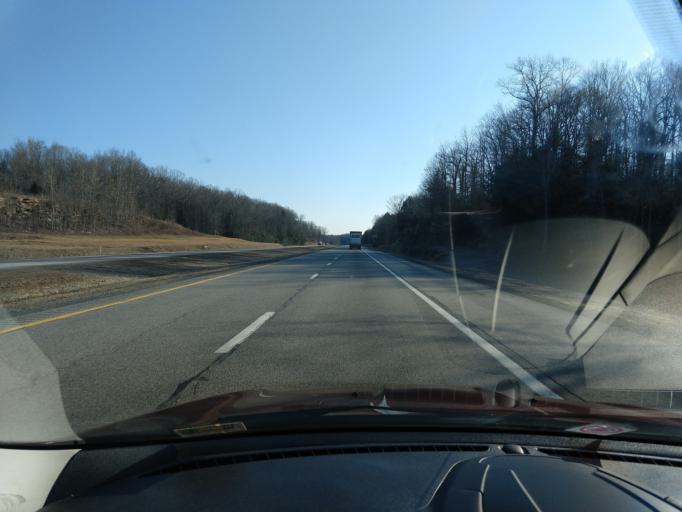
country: US
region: West Virginia
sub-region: Fayette County
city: Ansted
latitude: 38.1345
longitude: -80.9438
